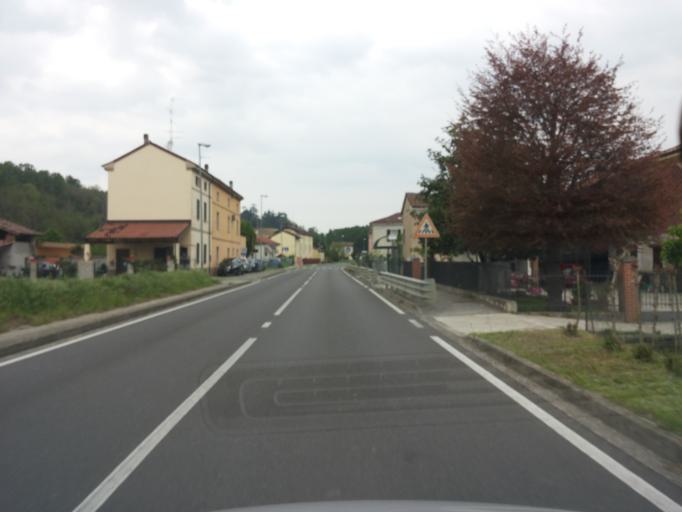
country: IT
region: Piedmont
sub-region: Provincia di Alessandria
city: Terruggia
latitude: 45.0892
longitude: 8.4651
